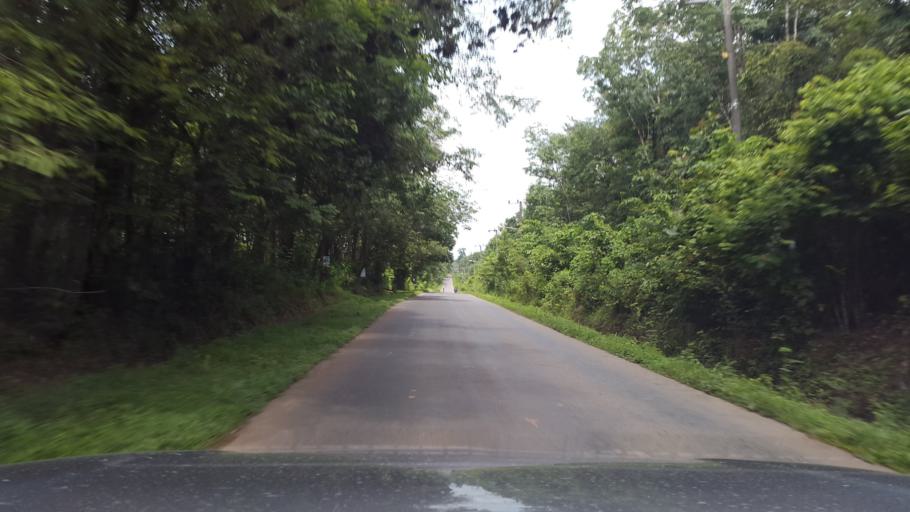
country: ID
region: South Sumatra
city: Gunungmegang Dalam
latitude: -3.3851
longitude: 103.9530
